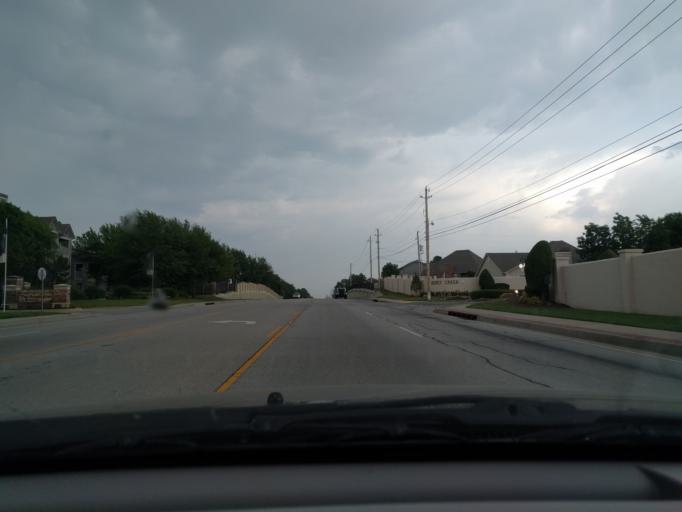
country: US
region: Oklahoma
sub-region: Tulsa County
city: Jenks
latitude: 36.0463
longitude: -95.8832
